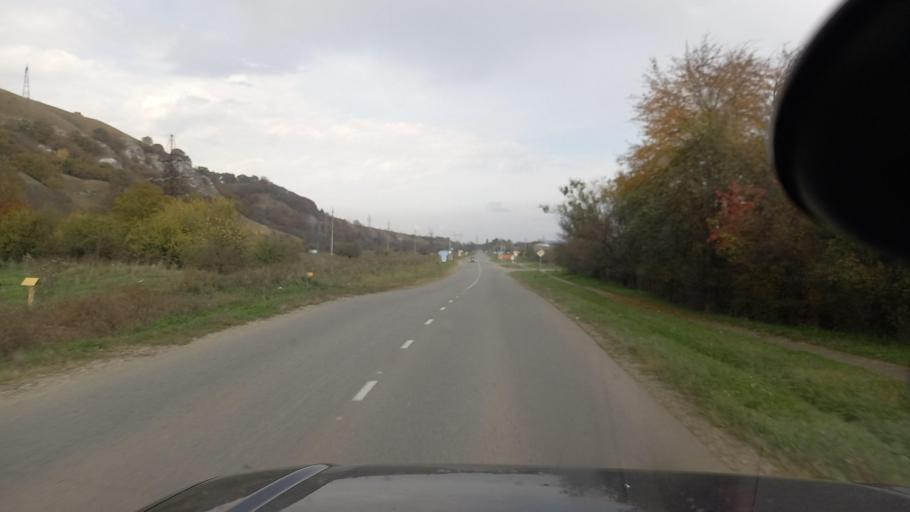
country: RU
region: Krasnodarskiy
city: Psebay
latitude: 44.1522
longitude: 40.8311
